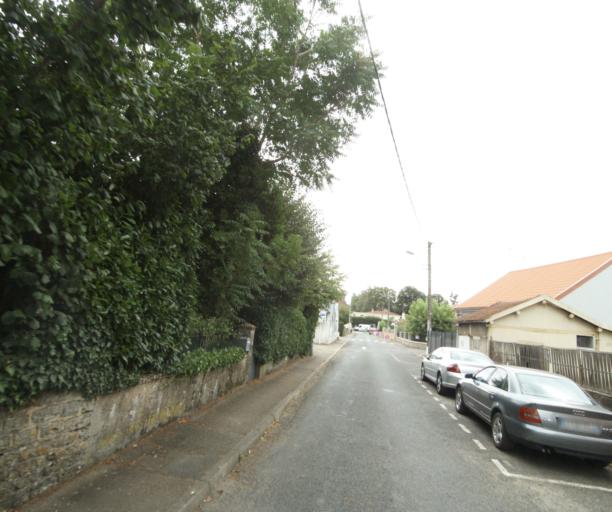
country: FR
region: Bourgogne
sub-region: Departement de Saone-et-Loire
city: Gueugnon
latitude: 46.6008
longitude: 4.0560
